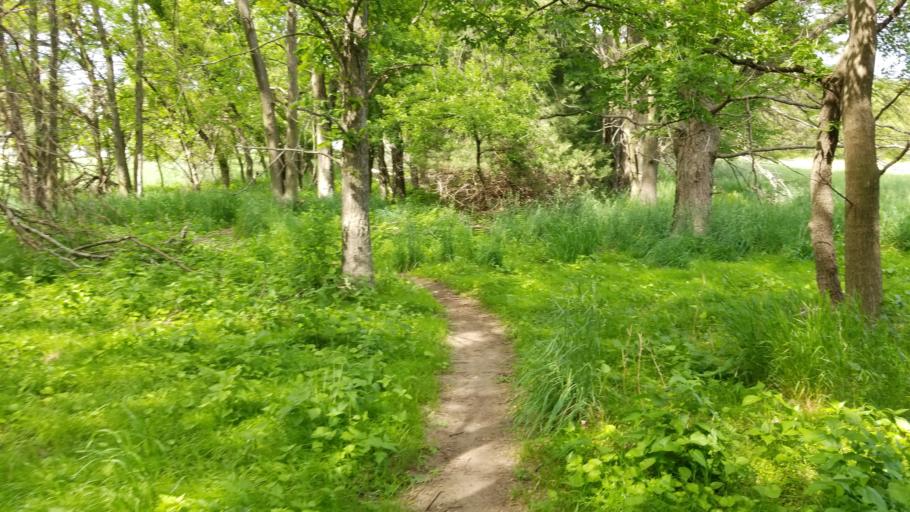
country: US
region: Nebraska
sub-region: Sarpy County
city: Chalco
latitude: 41.1721
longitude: -96.1656
